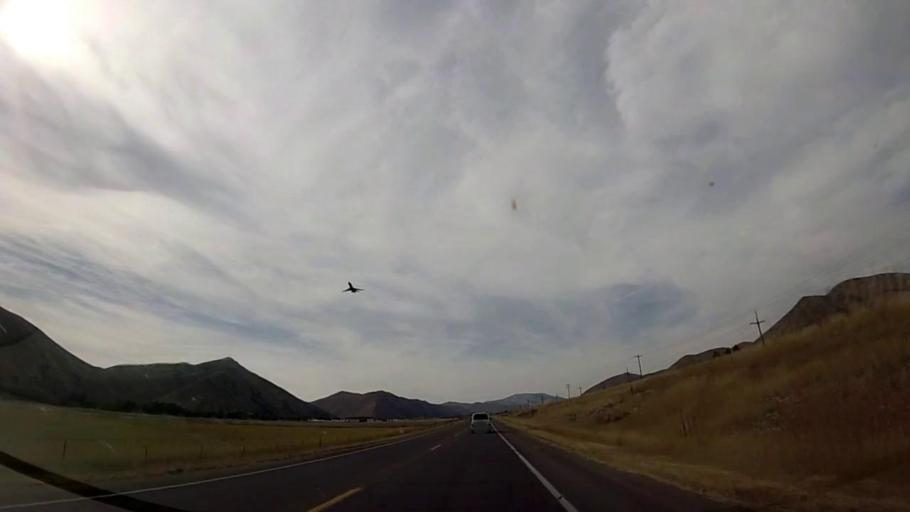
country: US
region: Idaho
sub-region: Blaine County
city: Bellevue
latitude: 43.4931
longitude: -114.2835
